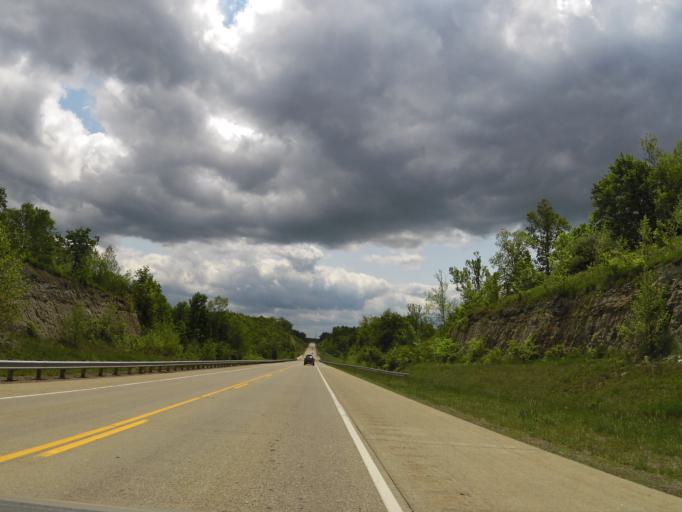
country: US
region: Ohio
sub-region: Meigs County
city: Pomeroy
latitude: 39.1750
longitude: -82.0444
